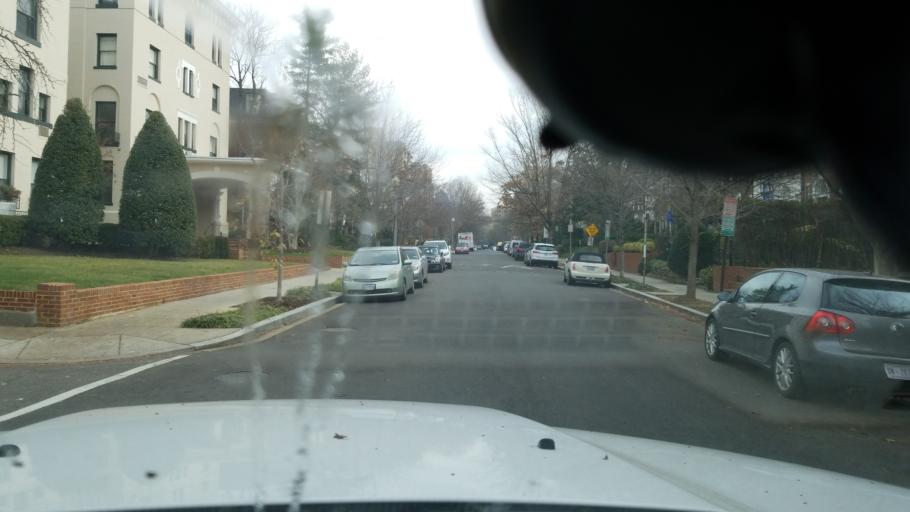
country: US
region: Washington, D.C.
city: Washington, D.C.
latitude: 38.9170
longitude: -77.0495
